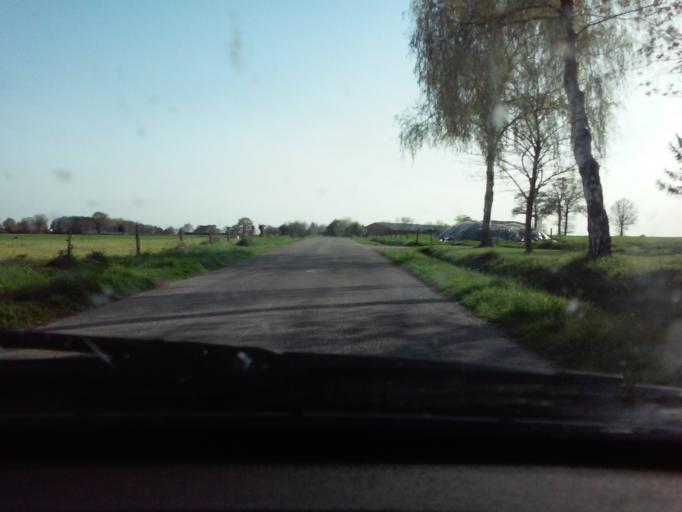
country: FR
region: Brittany
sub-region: Departement d'Ille-et-Vilaine
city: Romagne
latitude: 48.3051
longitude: -1.2640
